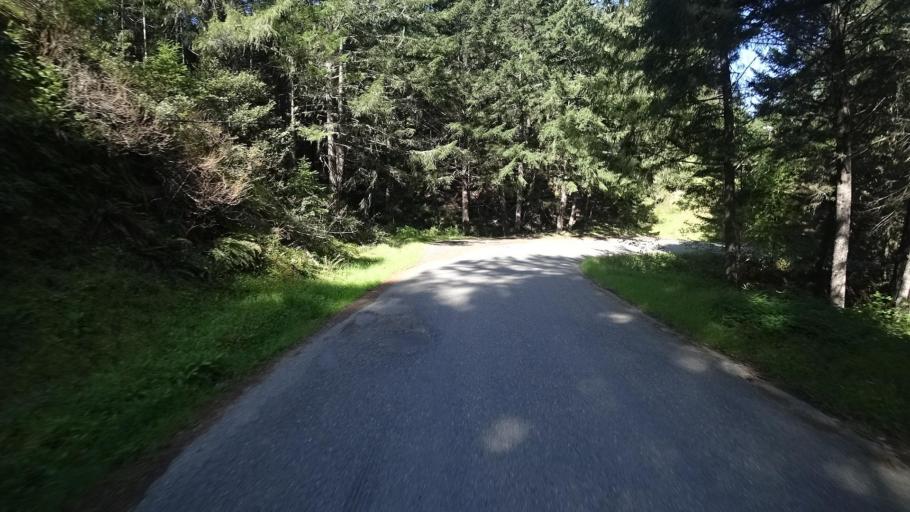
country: US
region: California
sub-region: Humboldt County
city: Redway
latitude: 40.0641
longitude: -123.6454
